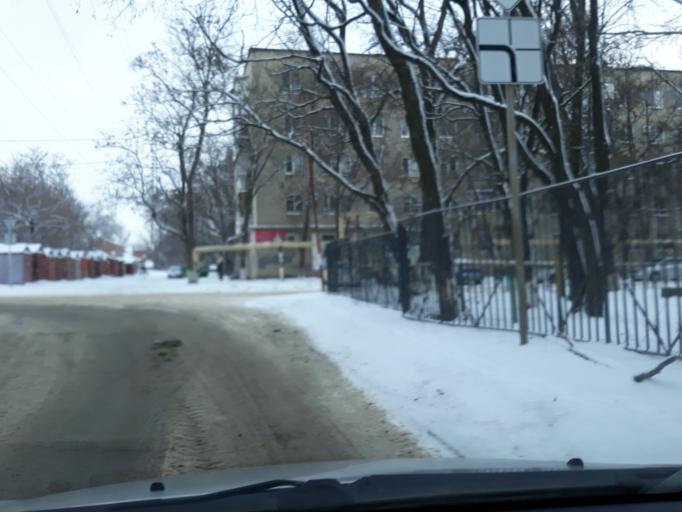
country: RU
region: Rostov
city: Taganrog
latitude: 47.2384
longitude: 38.8747
